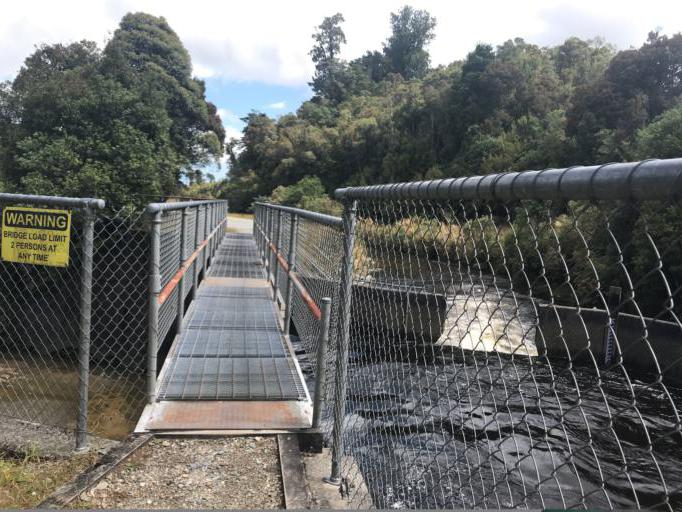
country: NZ
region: West Coast
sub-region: Westland District
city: Hokitika
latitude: -42.7556
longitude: 171.2248
